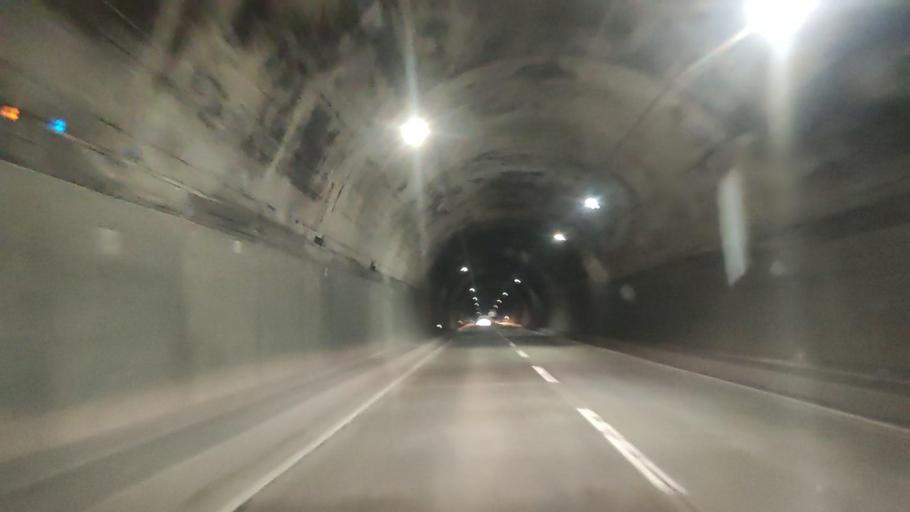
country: JP
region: Kagoshima
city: Okuchi-shinohara
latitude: 31.9757
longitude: 130.7414
